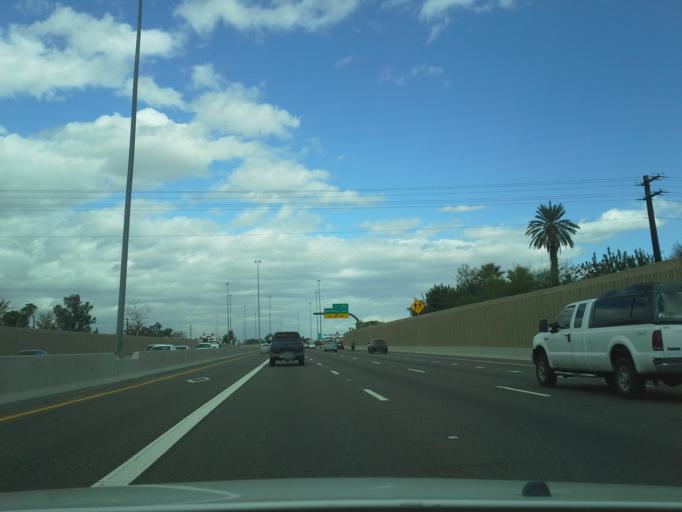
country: US
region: Arizona
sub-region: Maricopa County
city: Glendale
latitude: 33.5481
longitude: -112.1124
